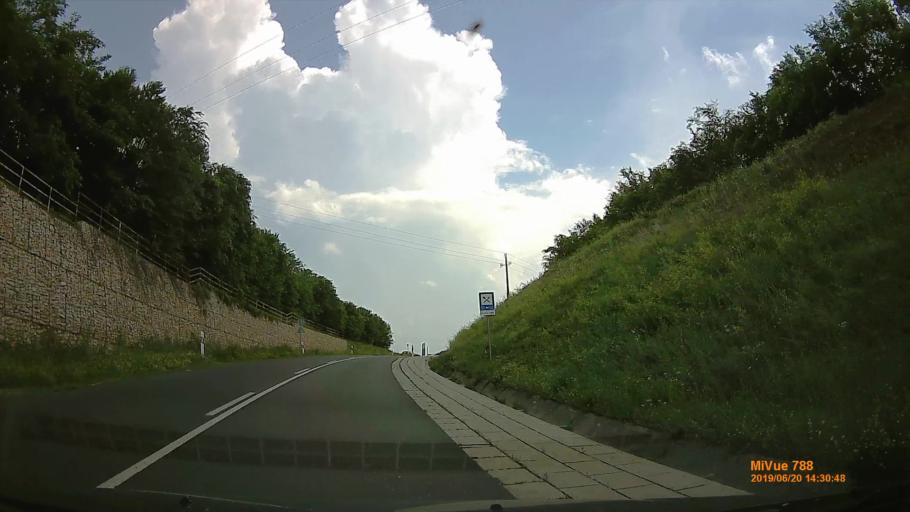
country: HU
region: Baranya
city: Hosszuheteny
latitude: 46.1456
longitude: 18.3482
